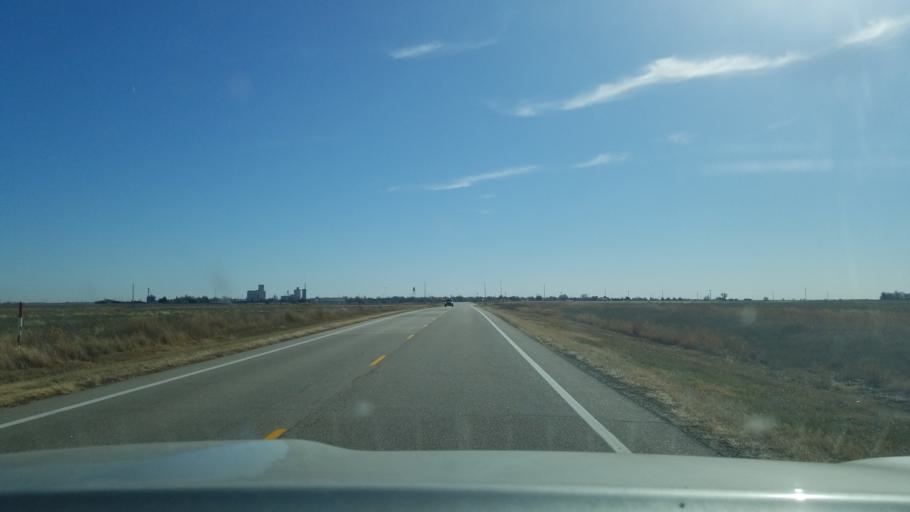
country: US
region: Kansas
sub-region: Kiowa County
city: Greensburg
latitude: 37.5614
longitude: -99.6517
